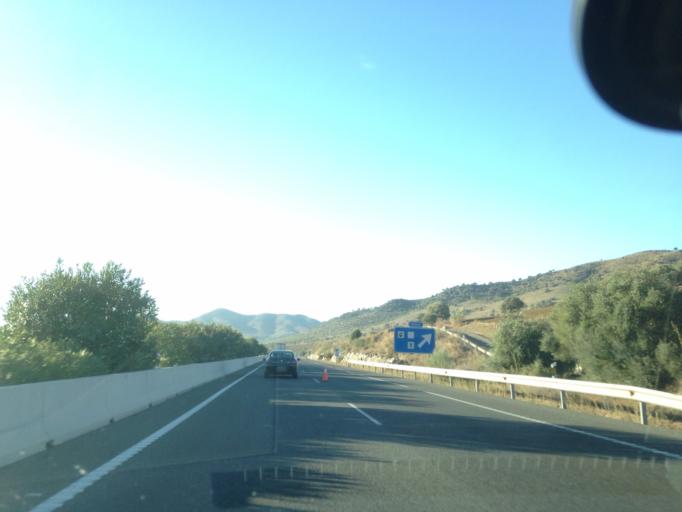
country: ES
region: Andalusia
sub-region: Provincia de Malaga
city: Casabermeja
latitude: 36.9307
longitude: -4.4463
